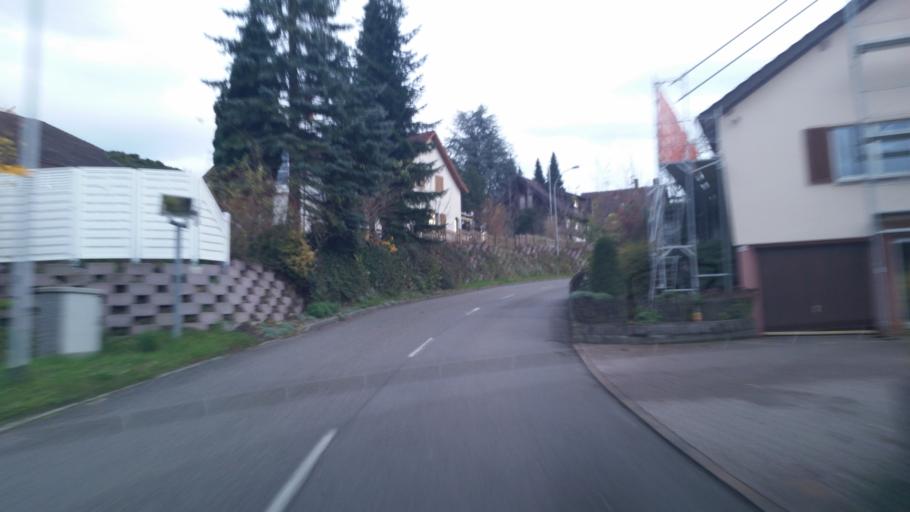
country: CH
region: Aargau
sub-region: Bezirk Baden
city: Kunten
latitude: 47.3893
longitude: 8.3343
